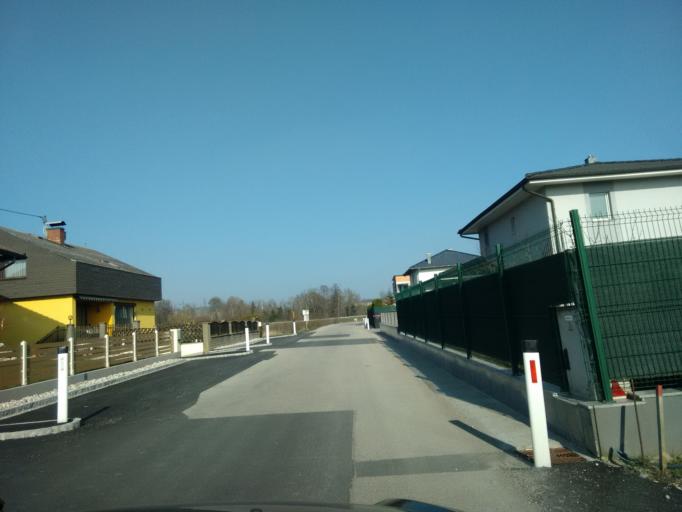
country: AT
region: Upper Austria
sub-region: Politischer Bezirk Grieskirchen
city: Bad Schallerbach
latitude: 48.2186
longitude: 13.9640
